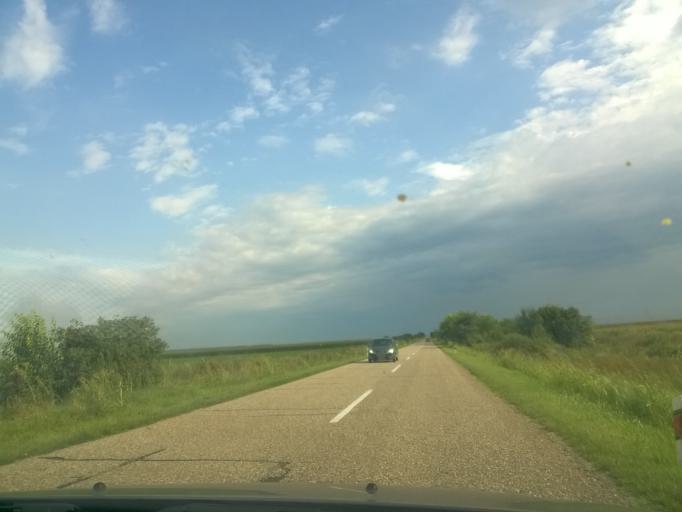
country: RS
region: Autonomna Pokrajina Vojvodina
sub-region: Juznobanatski Okrug
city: Kovacica
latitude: 45.1442
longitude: 20.6165
